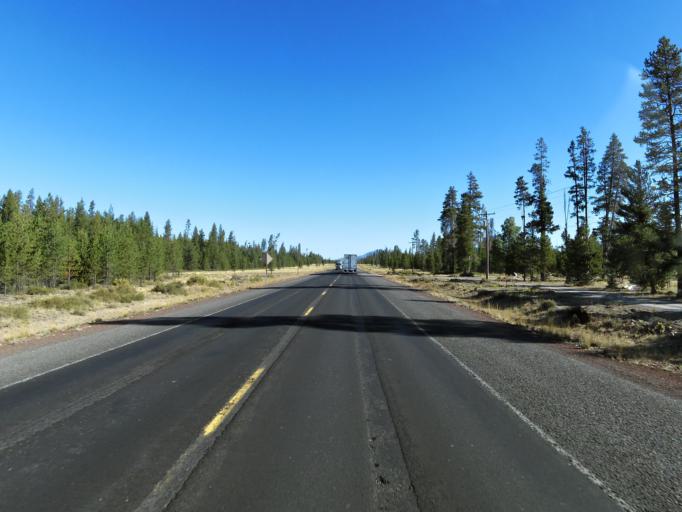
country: US
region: Oregon
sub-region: Deschutes County
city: La Pine
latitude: 43.1390
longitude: -121.8010
